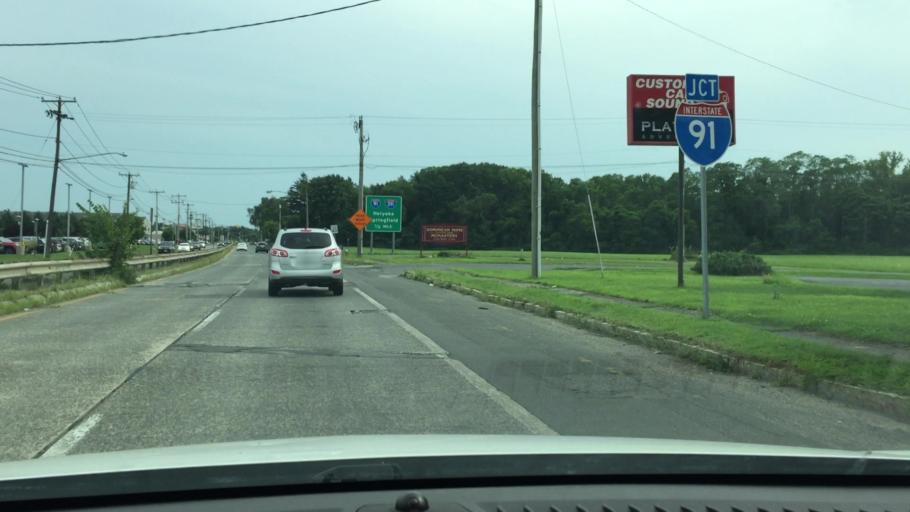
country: US
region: Massachusetts
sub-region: Hampden County
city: Chicopee
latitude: 42.1432
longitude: -72.6283
